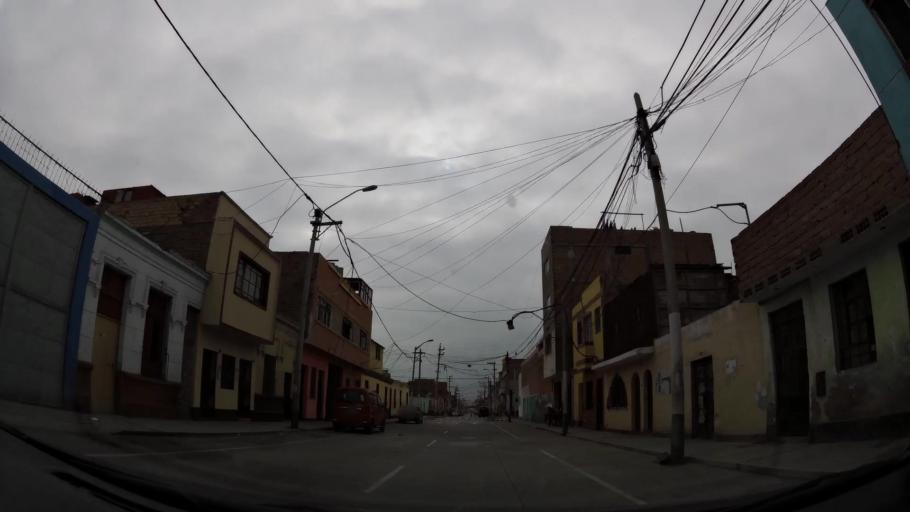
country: PE
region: Callao
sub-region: Callao
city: Callao
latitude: -12.0564
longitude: -77.1358
